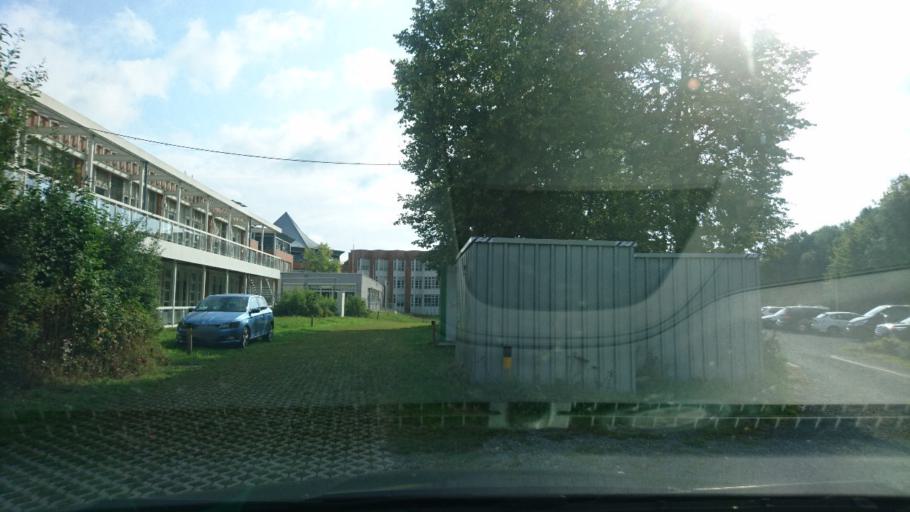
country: DE
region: Bavaria
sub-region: Upper Franconia
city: Heinersreuth
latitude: 49.9429
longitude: 11.5320
